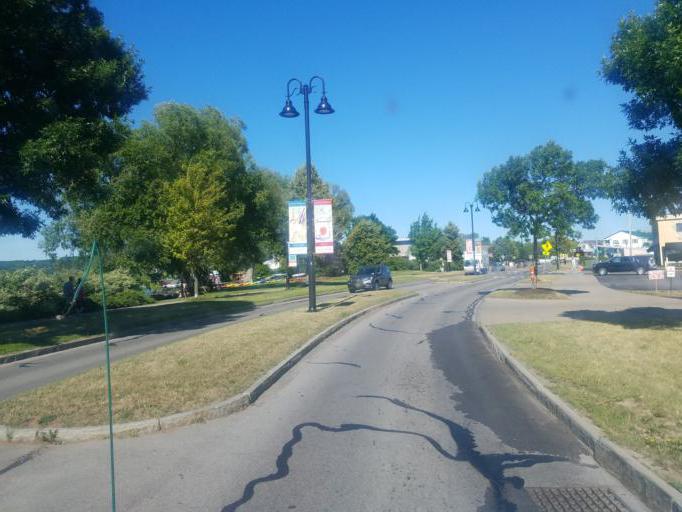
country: US
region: New York
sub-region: Ontario County
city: Canandaigua
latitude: 42.8756
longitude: -77.2702
